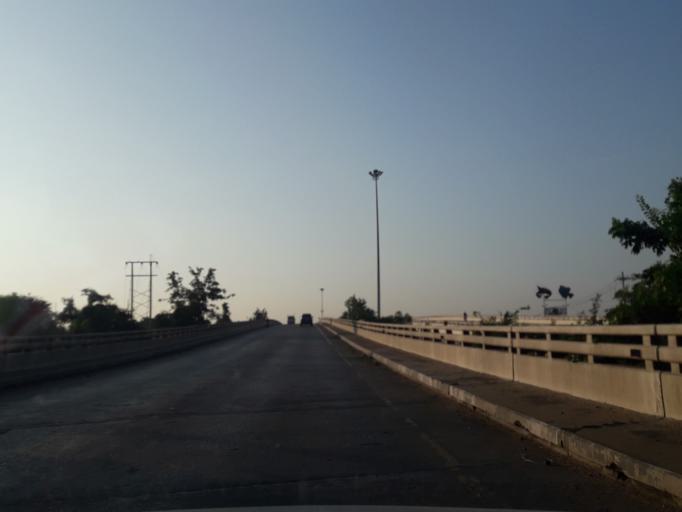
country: TH
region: Phra Nakhon Si Ayutthaya
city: Bang Pa-in
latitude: 14.1962
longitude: 100.5518
